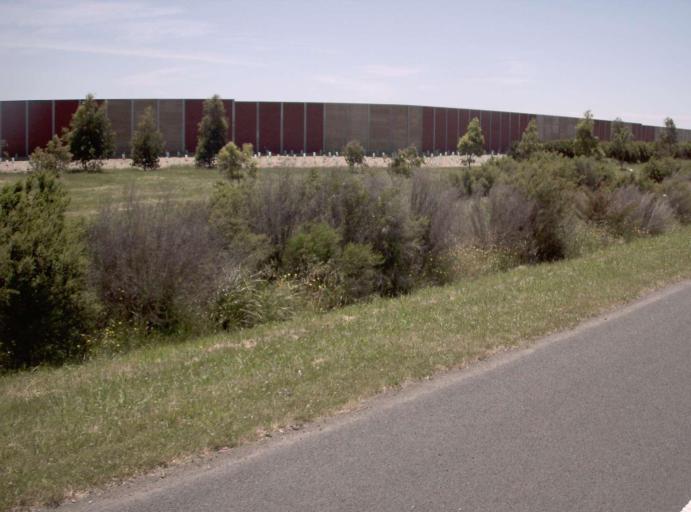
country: AU
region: Victoria
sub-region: Cardinia
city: Pakenham South
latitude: -38.0914
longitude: 145.4738
